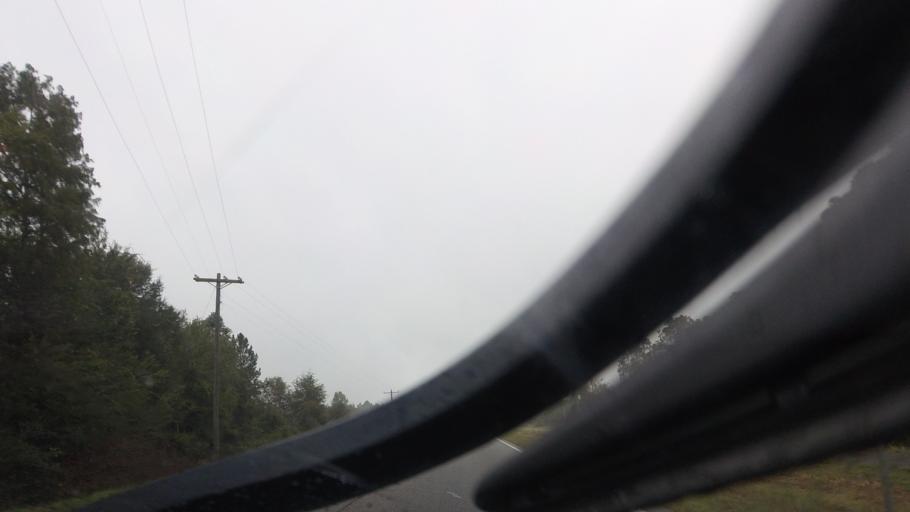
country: US
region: Georgia
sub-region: Ben Hill County
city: Fitzgerald
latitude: 31.7455
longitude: -83.2462
